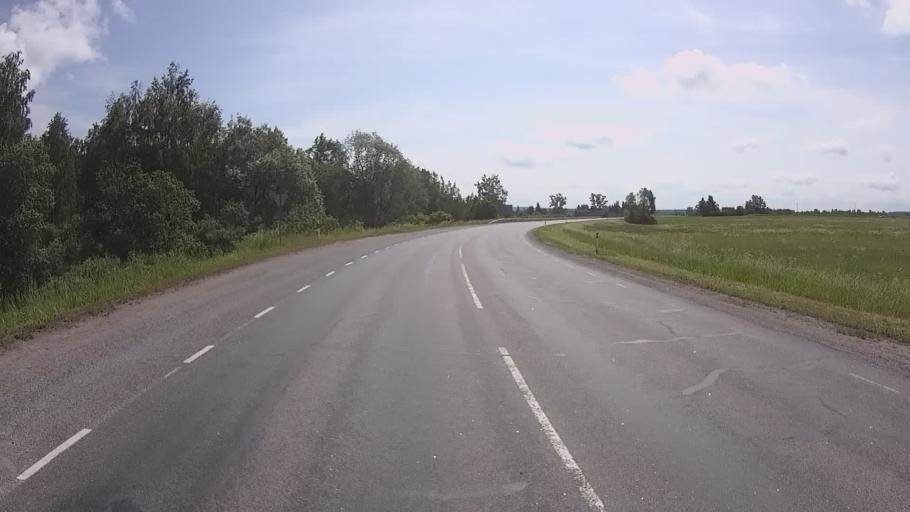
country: EE
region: Tartu
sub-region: UElenurme vald
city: Ulenurme
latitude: 58.2930
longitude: 26.7221
